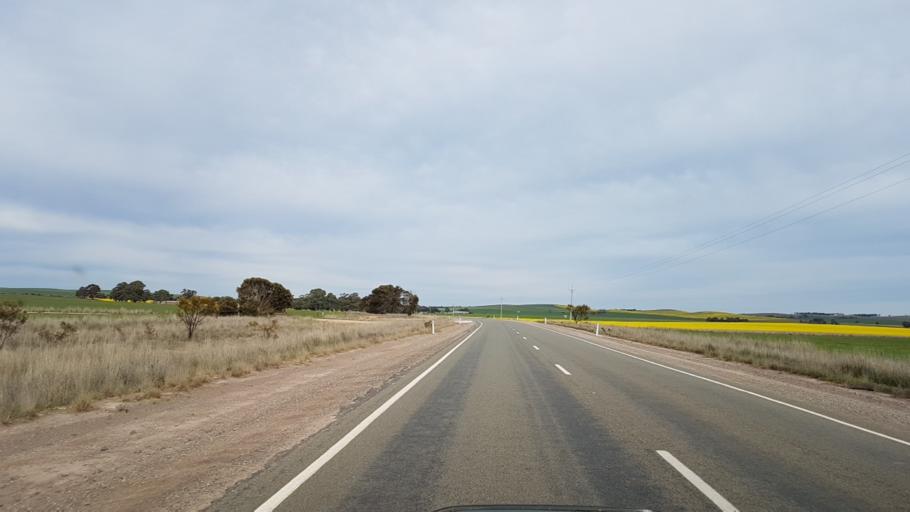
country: AU
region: South Australia
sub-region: Northern Areas
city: Jamestown
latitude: -33.1967
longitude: 138.5212
